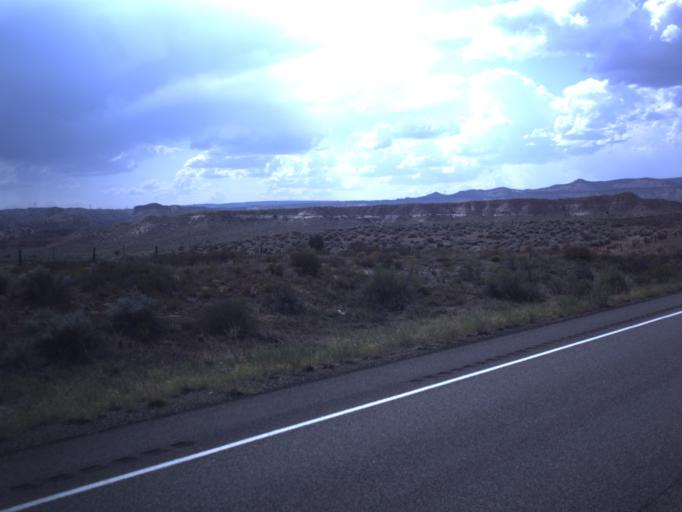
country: US
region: Arizona
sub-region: Coconino County
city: Page
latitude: 37.1034
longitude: -111.8839
